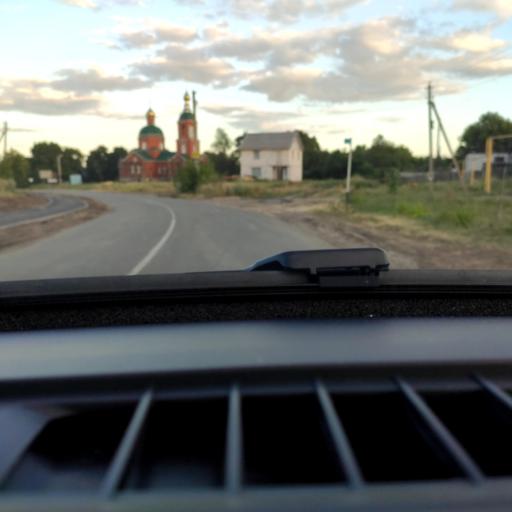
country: RU
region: Voronezj
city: Orlovo
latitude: 51.6552
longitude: 39.7036
